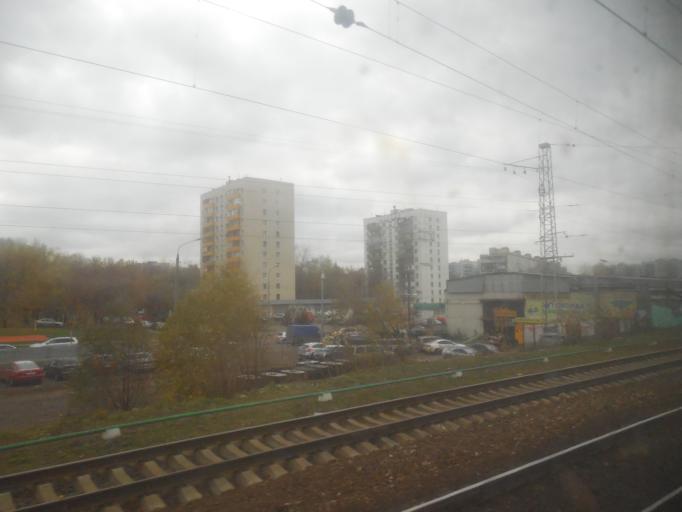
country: RU
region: Moskovskaya
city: Bol'shaya Setun'
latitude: 55.7268
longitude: 37.4363
